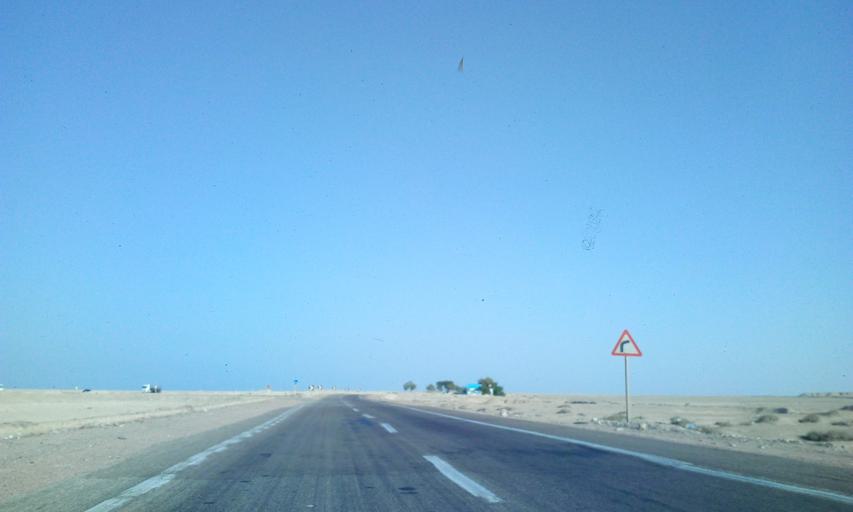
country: EG
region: As Suways
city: Ain Sukhna
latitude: 28.8429
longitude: 32.7015
